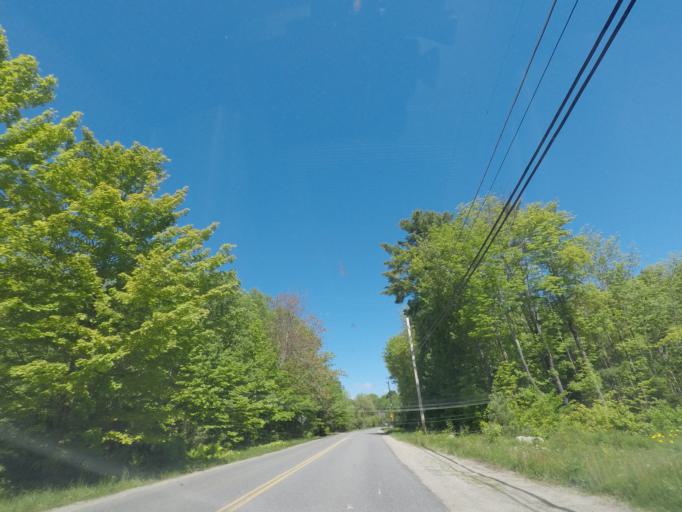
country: US
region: Maine
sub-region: Kennebec County
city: Manchester
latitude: 44.2374
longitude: -69.8888
